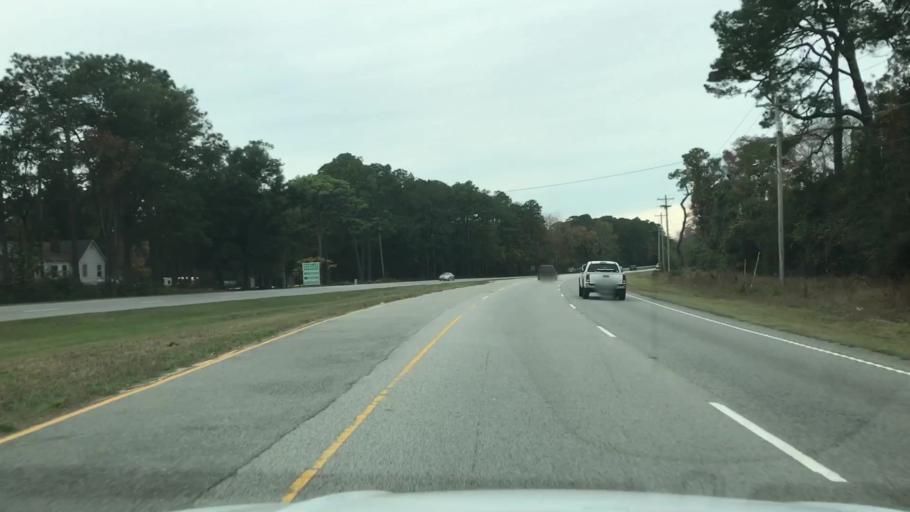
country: US
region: South Carolina
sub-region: Georgetown County
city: Georgetown
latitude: 33.3648
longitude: -79.2260
